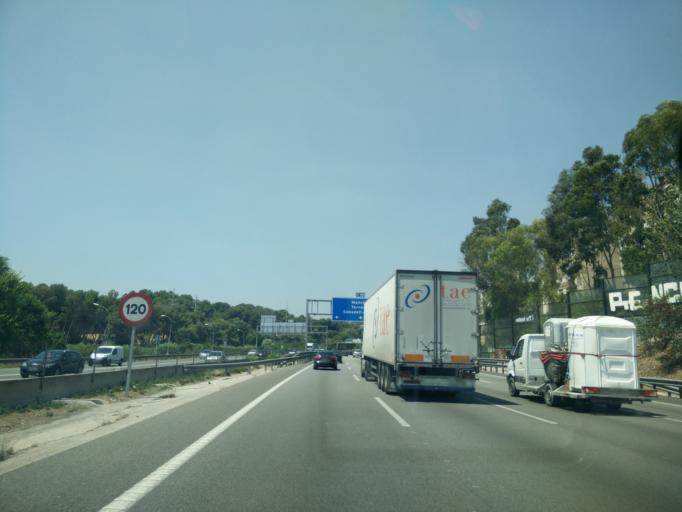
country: ES
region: Catalonia
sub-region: Provincia de Barcelona
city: Barbera del Valles
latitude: 41.5047
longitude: 2.1176
